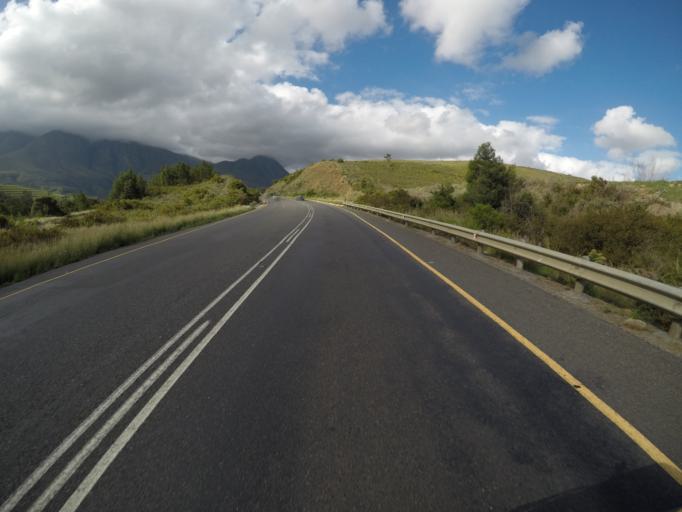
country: ZA
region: Western Cape
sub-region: Overberg District Municipality
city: Swellendam
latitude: -34.0024
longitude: 20.3350
